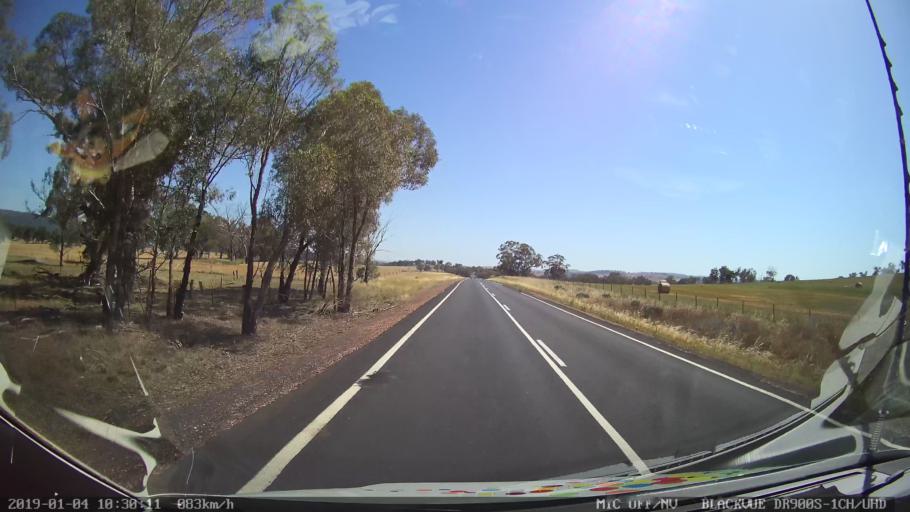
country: AU
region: New South Wales
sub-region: Cabonne
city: Canowindra
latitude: -33.3487
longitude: 148.6264
